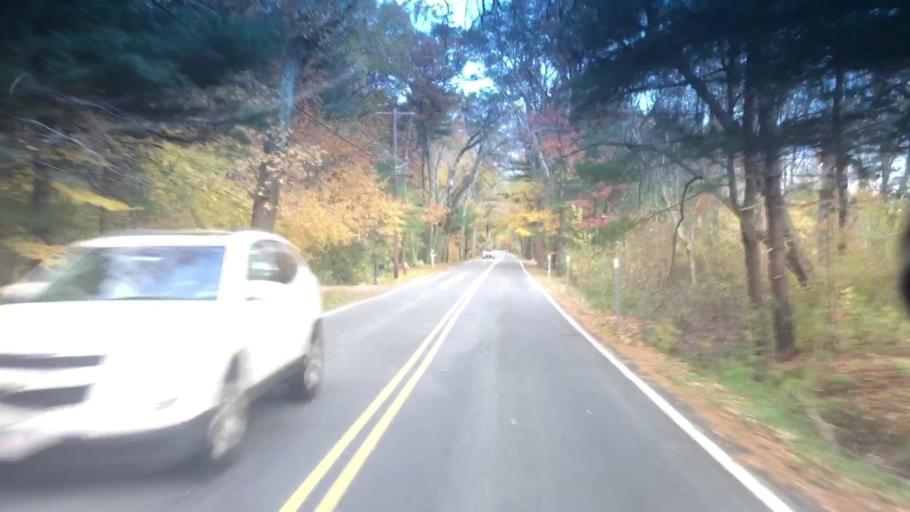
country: US
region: Massachusetts
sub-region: Norfolk County
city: Medfield
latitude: 42.2008
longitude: -71.2795
